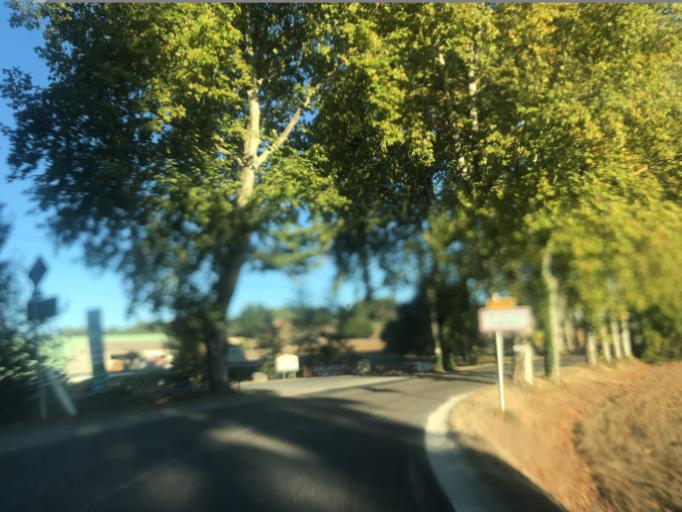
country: FR
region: Poitou-Charentes
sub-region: Departement de la Charente-Maritime
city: Saint-Aigulin
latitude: 45.1577
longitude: 0.0028
